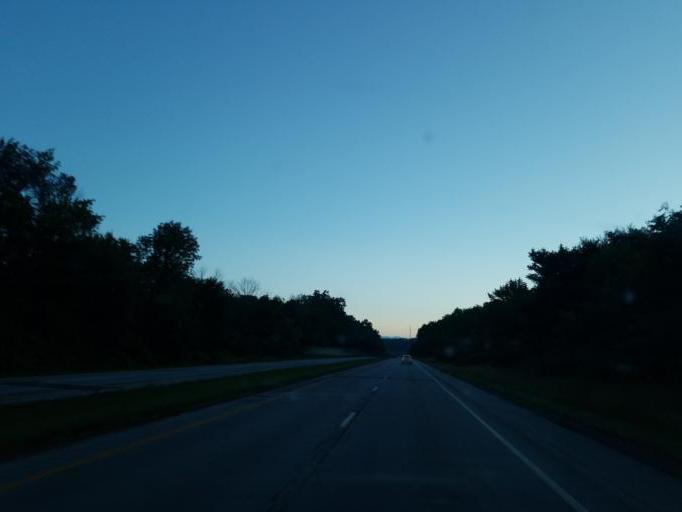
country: US
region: Ohio
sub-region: Summit County
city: Clinton
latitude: 40.9105
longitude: -81.6482
